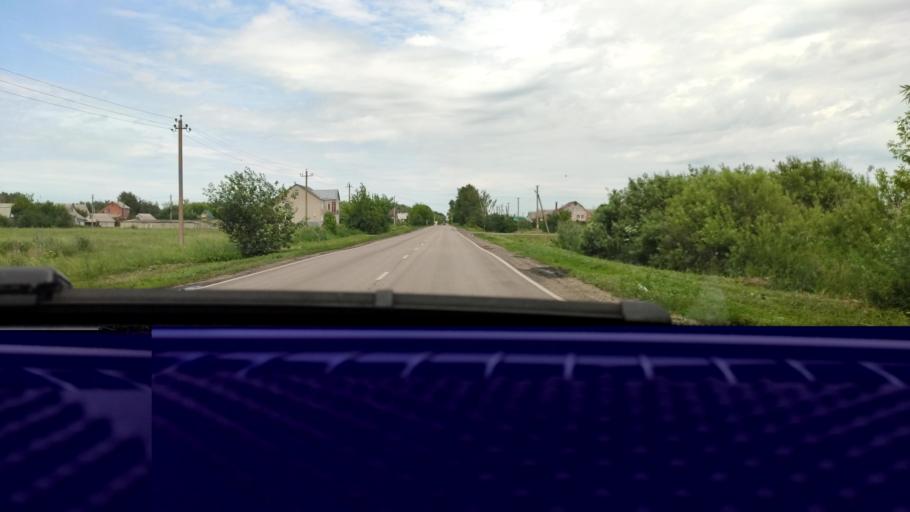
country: RU
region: Voronezj
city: Panino
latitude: 51.6517
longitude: 40.1156
